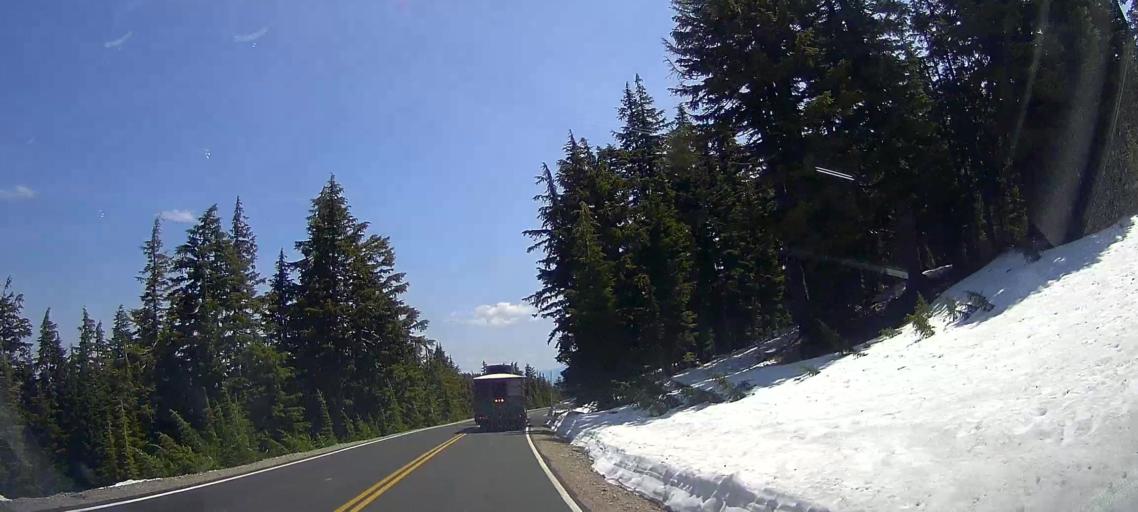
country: US
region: Oregon
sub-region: Jackson County
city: Shady Cove
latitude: 42.9819
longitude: -122.1359
